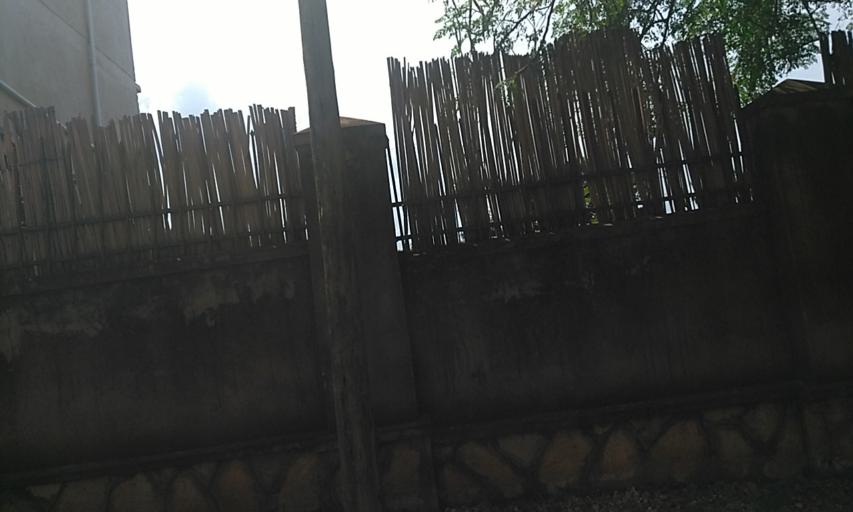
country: UG
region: Central Region
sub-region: Wakiso District
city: Kireka
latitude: 0.3483
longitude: 32.6154
